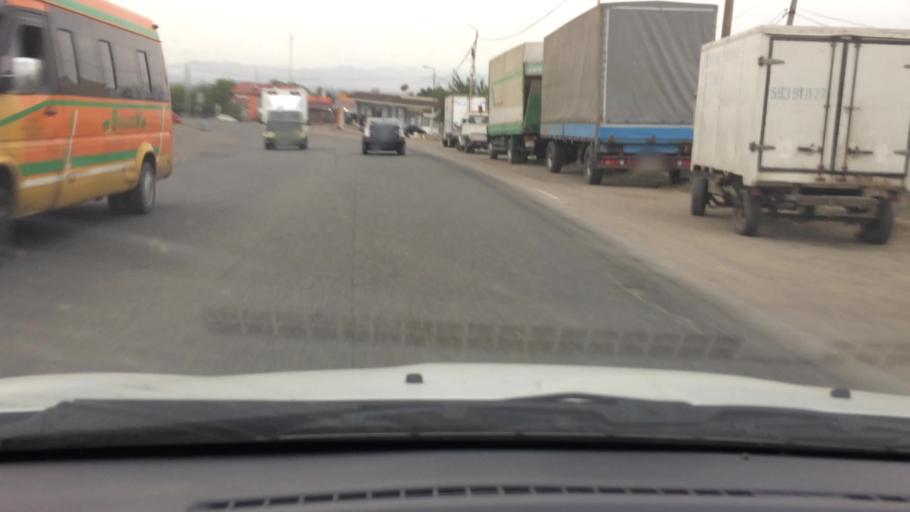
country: GE
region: Kvemo Kartli
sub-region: Marneuli
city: Marneuli
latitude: 41.4956
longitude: 44.8020
